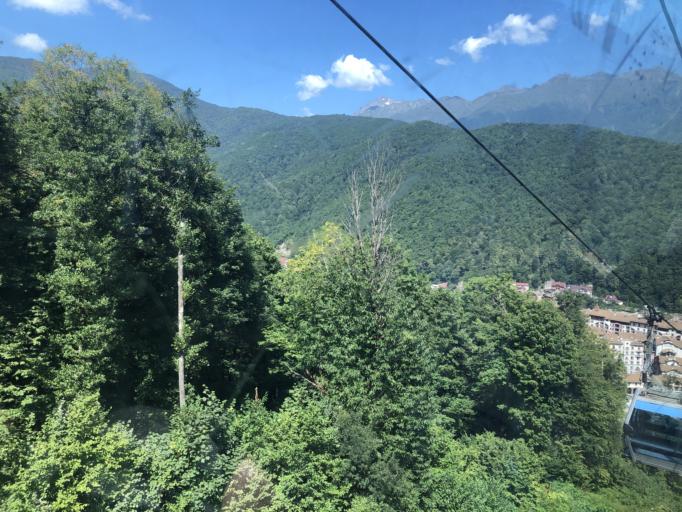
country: RU
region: Krasnodarskiy
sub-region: Sochi City
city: Krasnaya Polyana
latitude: 43.6790
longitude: 40.2646
